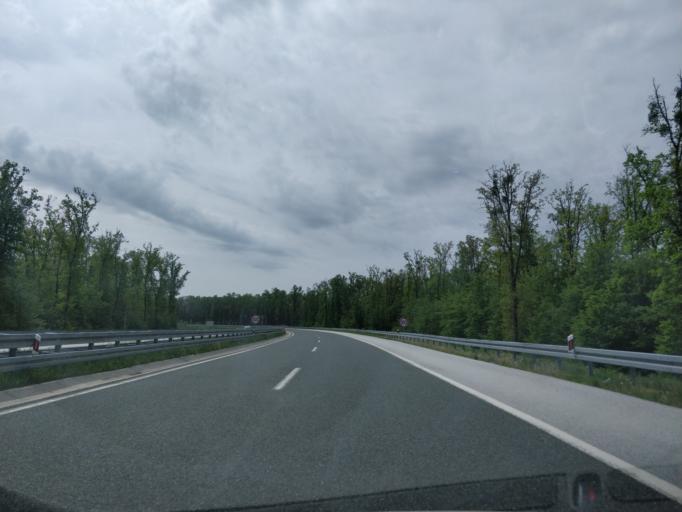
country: HR
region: Zagrebacka
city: Mraclin
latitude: 45.6300
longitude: 16.0965
